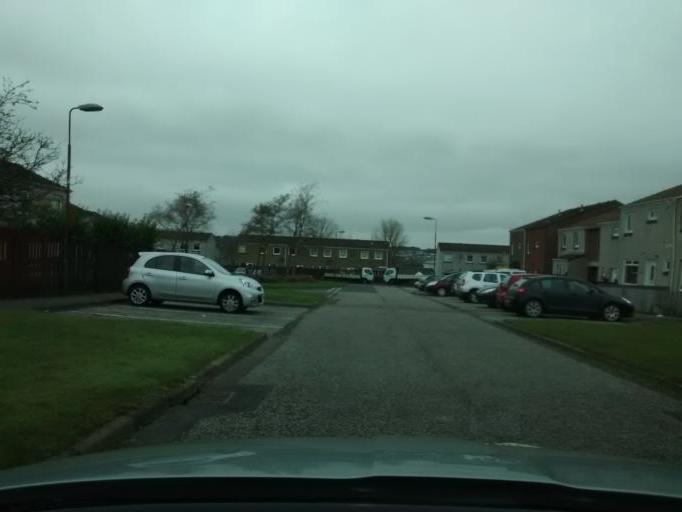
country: GB
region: Scotland
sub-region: West Lothian
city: Livingston
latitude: 55.8793
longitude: -3.5061
